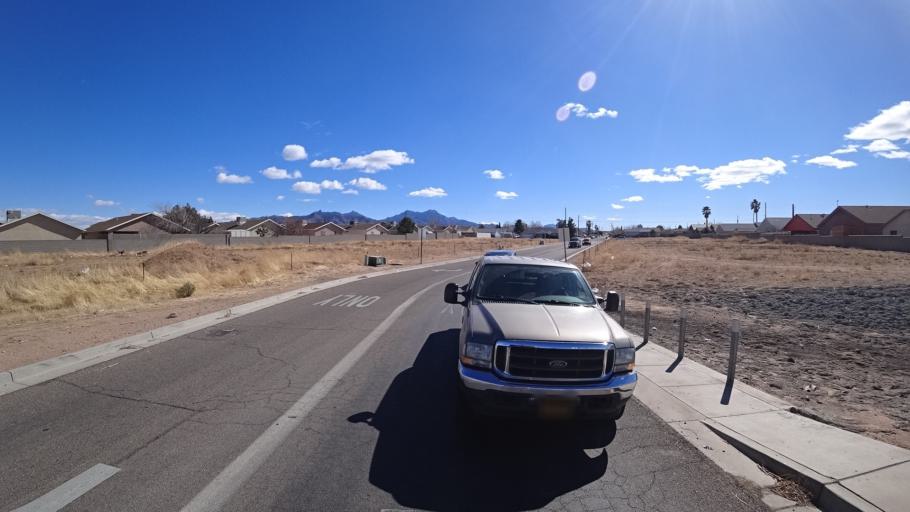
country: US
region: Arizona
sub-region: Mohave County
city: New Kingman-Butler
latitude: 35.2223
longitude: -113.9986
